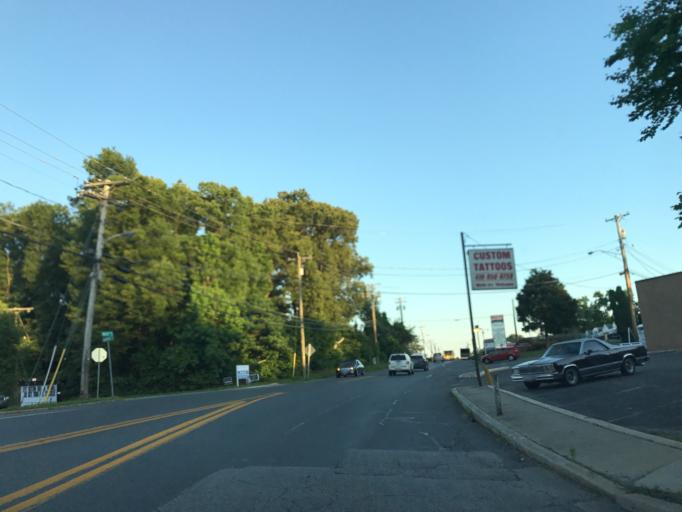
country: US
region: Maryland
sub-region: Anne Arundel County
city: Londontowne
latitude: 38.9373
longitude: -76.5588
